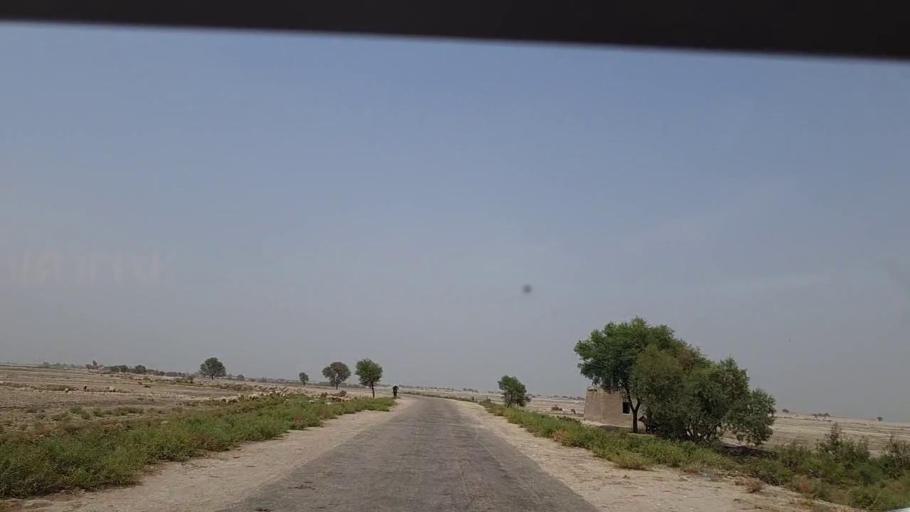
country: PK
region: Sindh
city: Khairpur Nathan Shah
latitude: 27.0551
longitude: 67.6469
